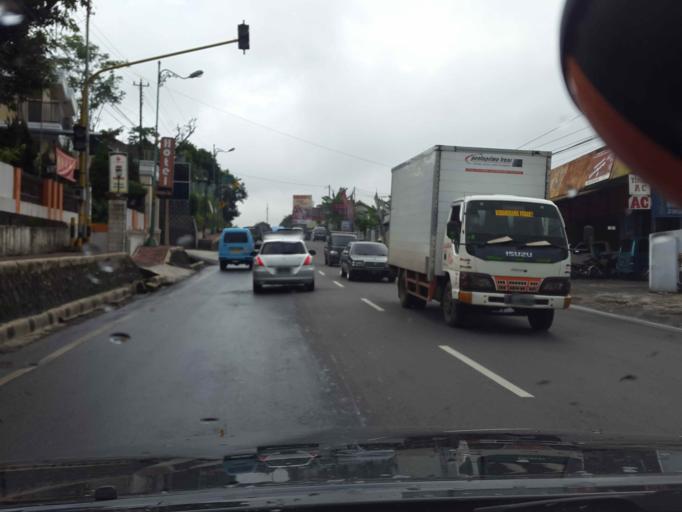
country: ID
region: Central Java
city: Salatiga
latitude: -7.3082
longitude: 110.4897
